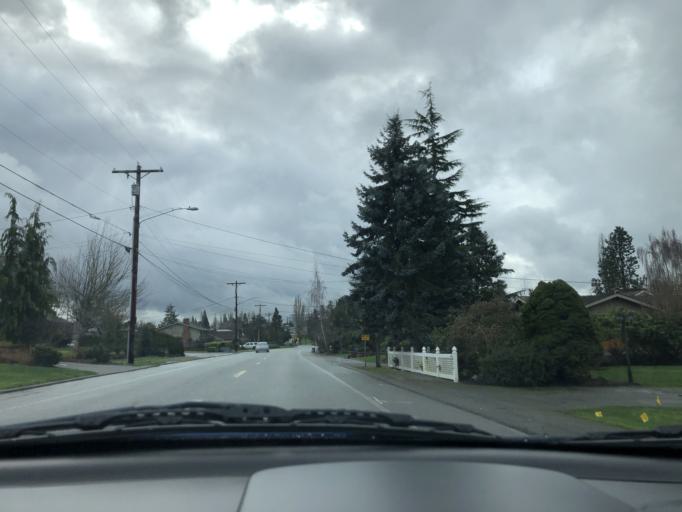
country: US
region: Washington
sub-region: Snohomish County
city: Everett
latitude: 48.0144
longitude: -122.2049
